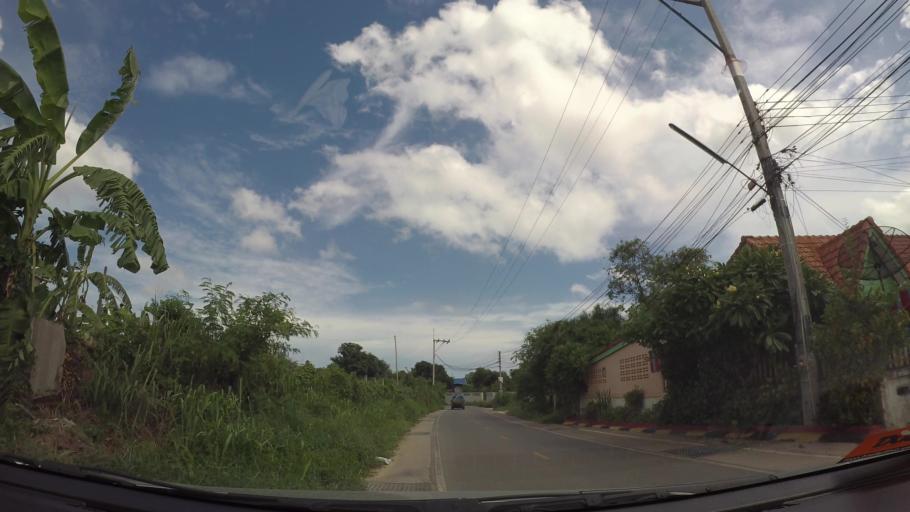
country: TH
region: Chon Buri
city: Sattahip
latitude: 12.6897
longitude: 100.9014
